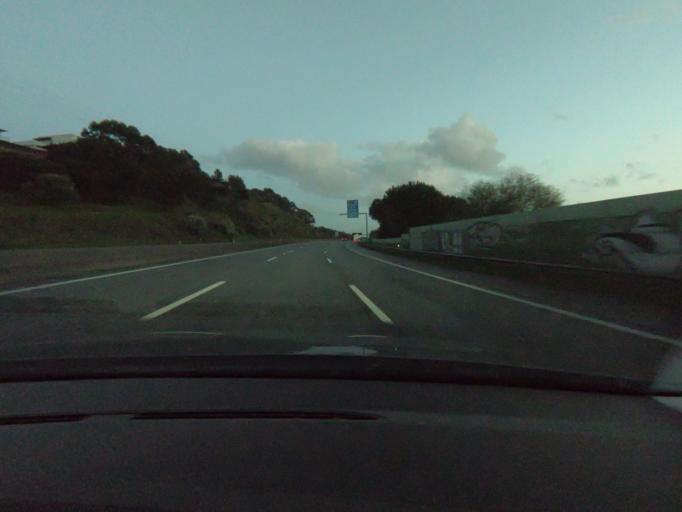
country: PT
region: Lisbon
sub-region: Oeiras
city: Barcarena
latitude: 38.7319
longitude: -9.2748
